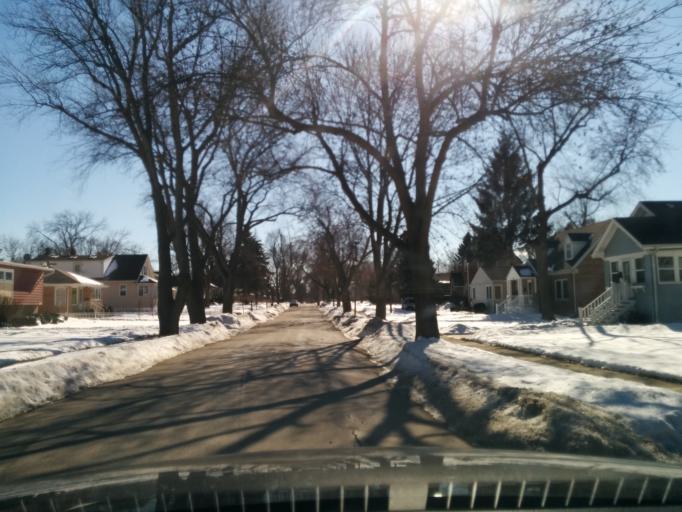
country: US
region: Illinois
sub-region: DuPage County
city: Villa Park
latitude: 41.8956
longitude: -87.9679
